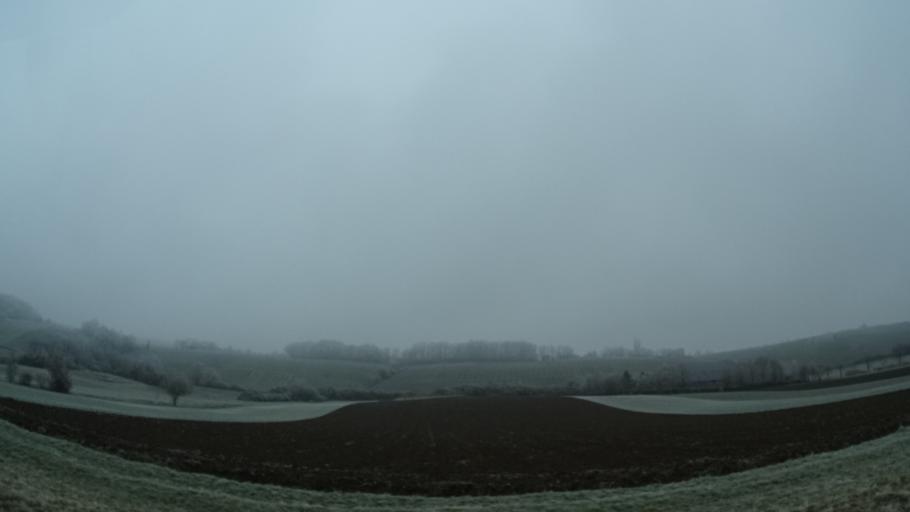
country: DE
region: Bavaria
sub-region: Regierungsbezirk Unterfranken
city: Sulzfeld am Main
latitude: 49.6994
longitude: 10.1255
